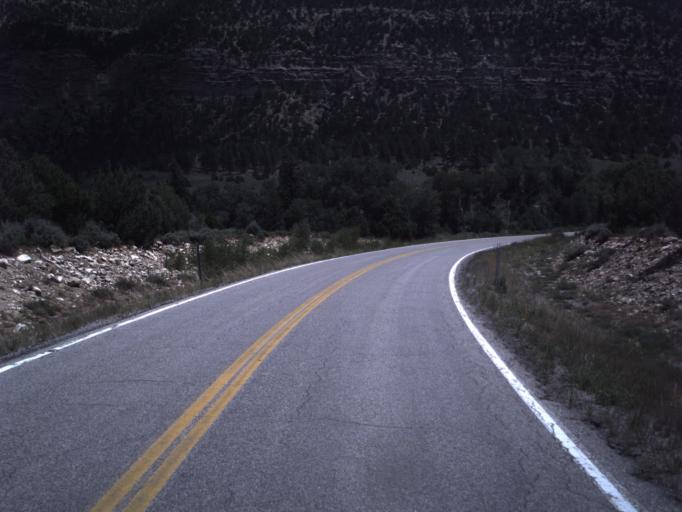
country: US
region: Utah
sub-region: Emery County
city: Orangeville
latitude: 39.3230
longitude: -111.2789
